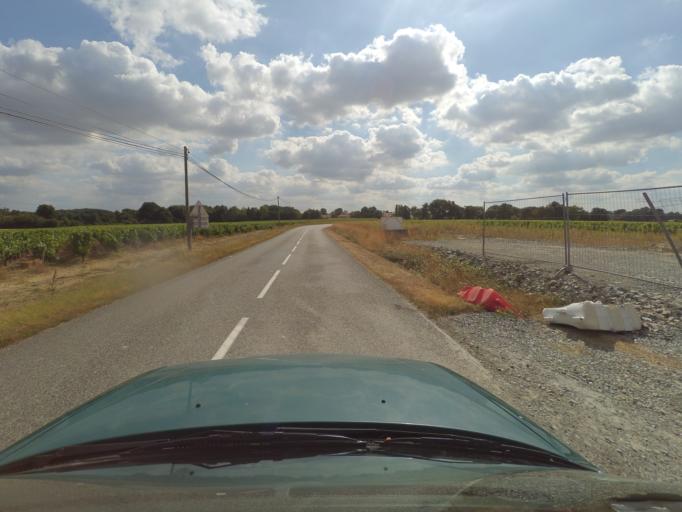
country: FR
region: Pays de la Loire
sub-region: Departement de la Loire-Atlantique
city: Aigrefeuille-sur-Maine
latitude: 47.0656
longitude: -1.4047
